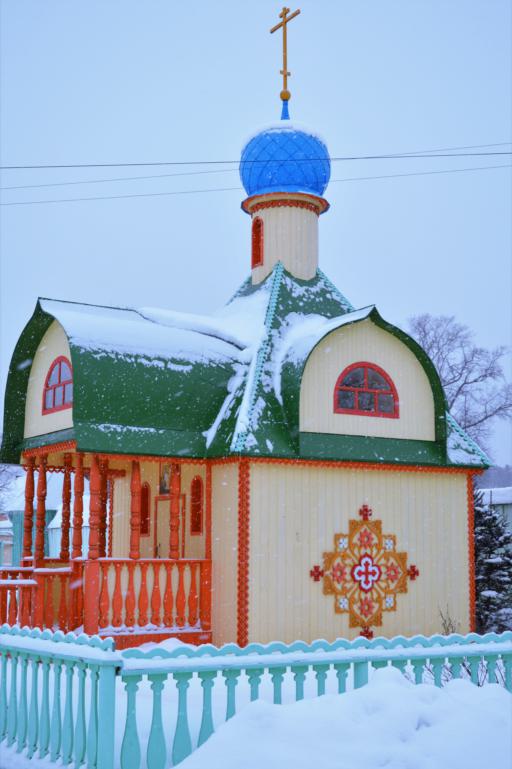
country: RU
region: Kirov
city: Darovskoy
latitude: 58.9146
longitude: 48.0074
